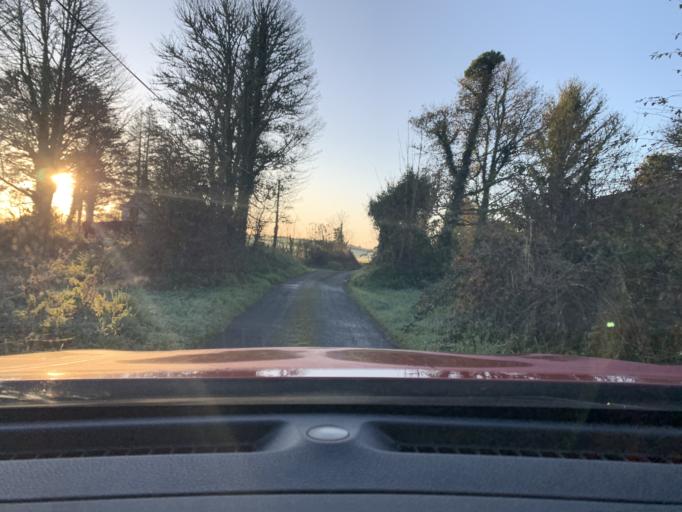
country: IE
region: Connaught
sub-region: Sligo
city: Ballymote
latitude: 54.0610
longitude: -8.5184
